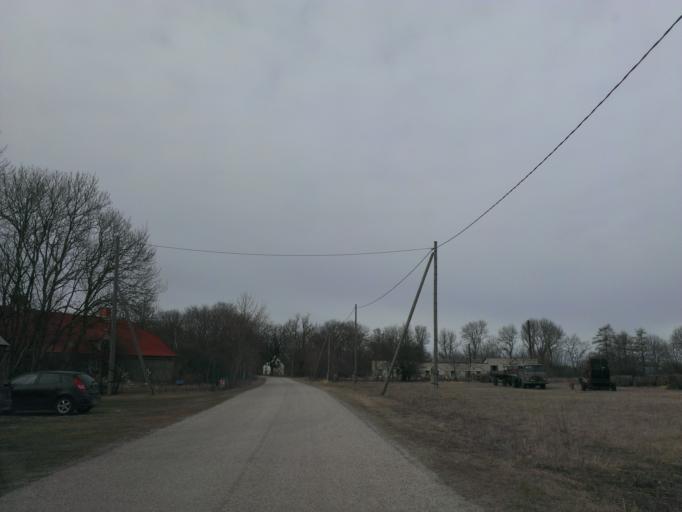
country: EE
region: Laeaene
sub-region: Lihula vald
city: Lihula
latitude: 58.5799
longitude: 23.5404
